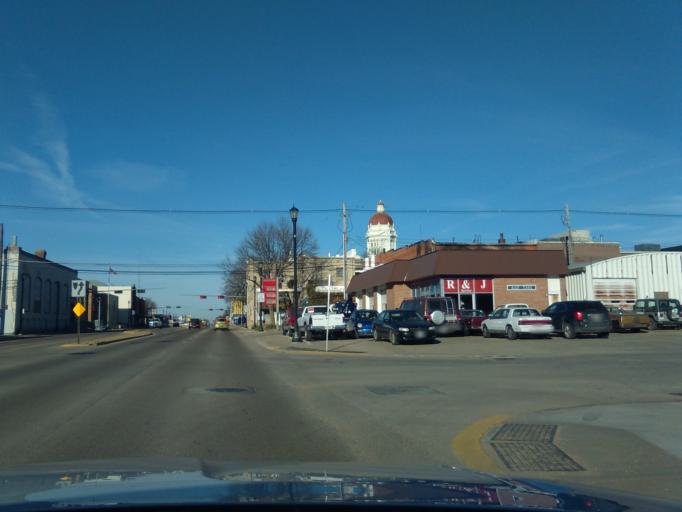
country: US
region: Nebraska
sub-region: Seward County
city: Seward
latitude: 40.9070
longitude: -97.0965
